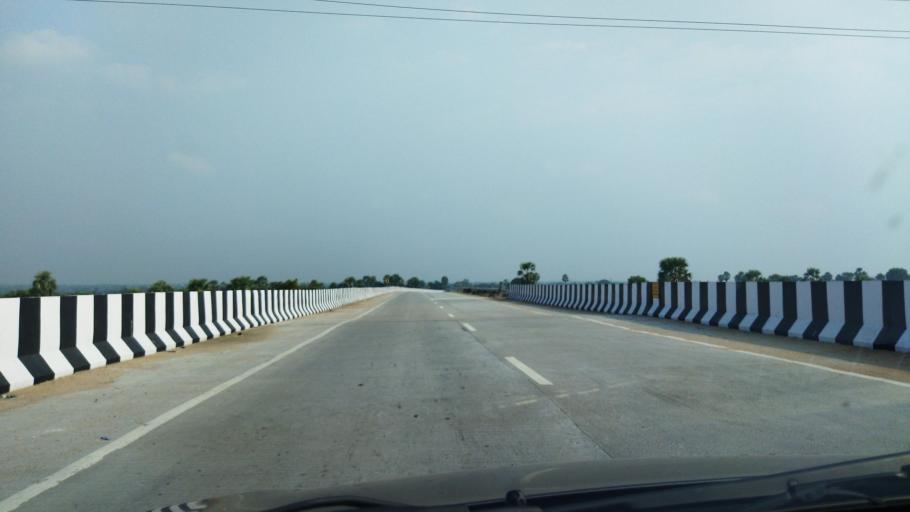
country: IN
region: Telangana
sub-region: Nalgonda
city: Nalgonda
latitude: 17.1687
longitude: 79.3951
